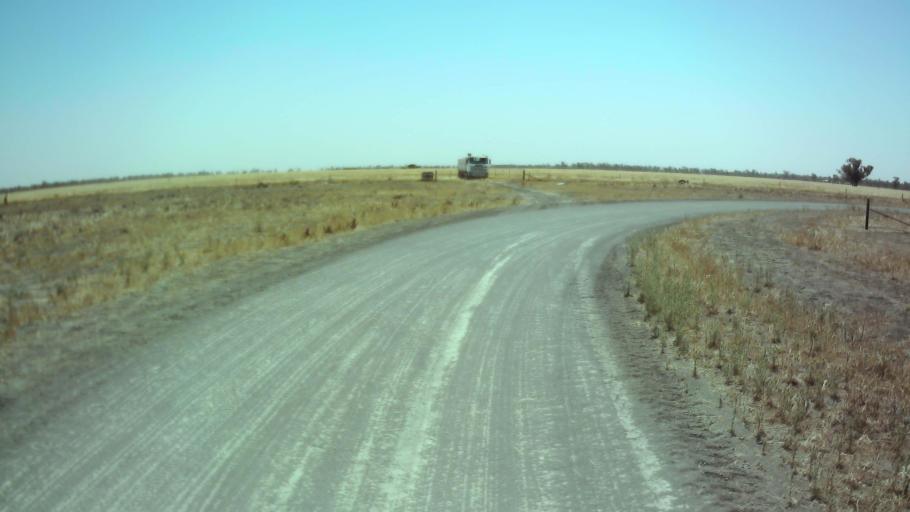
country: AU
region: New South Wales
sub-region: Weddin
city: Grenfell
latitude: -33.9954
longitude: 147.8659
